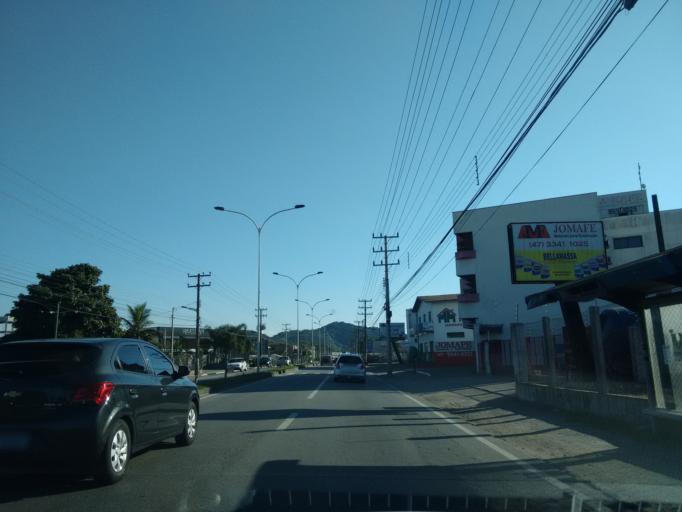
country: BR
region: Santa Catarina
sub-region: Itajai
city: Itajai
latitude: -26.8884
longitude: -48.7072
